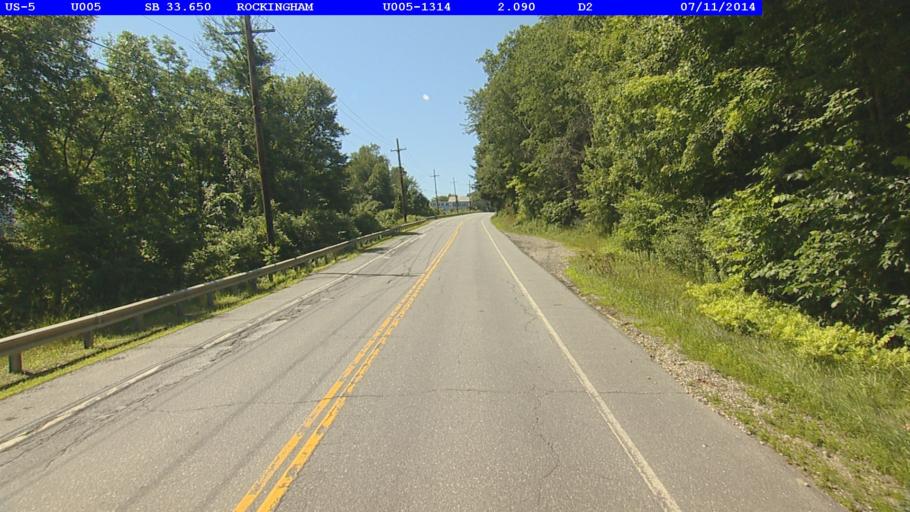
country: US
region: Vermont
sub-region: Windham County
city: Bellows Falls
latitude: 43.1514
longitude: -72.4589
